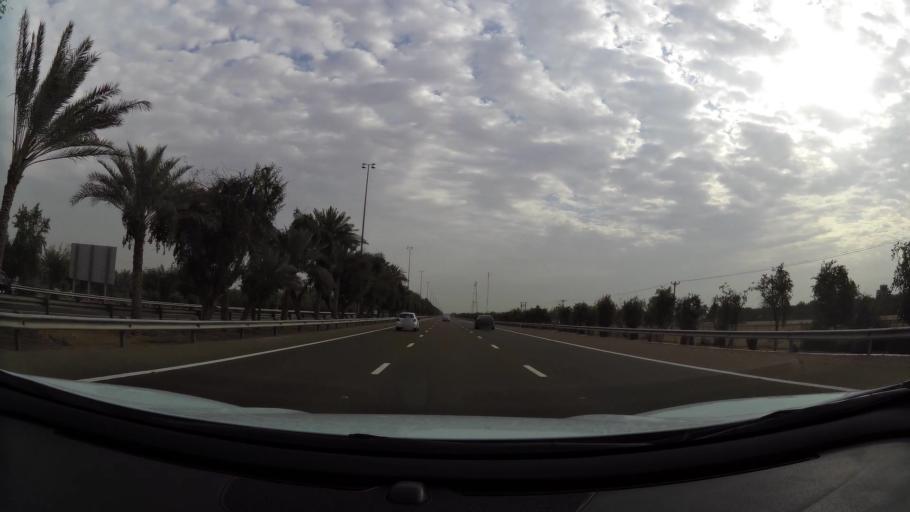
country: AE
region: Abu Dhabi
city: Al Ain
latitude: 24.1858
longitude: 55.3418
